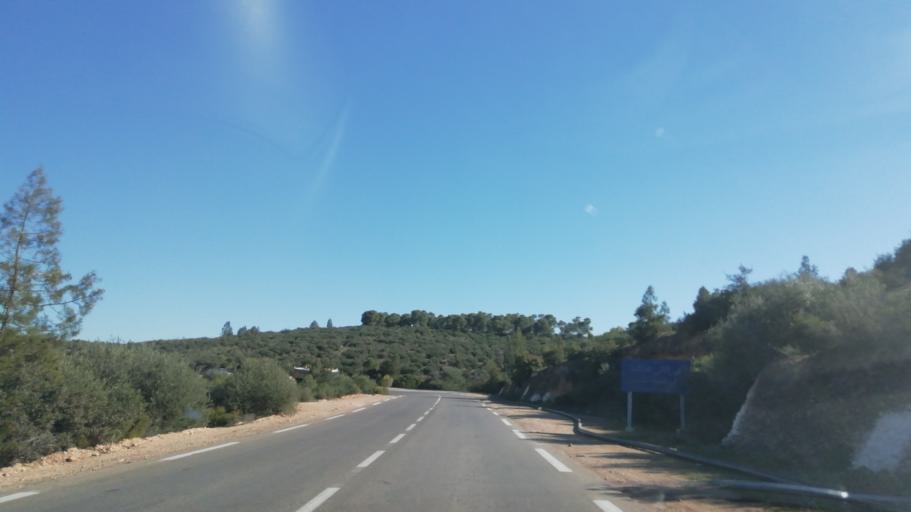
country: DZ
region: Tlemcen
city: Beni Mester
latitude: 34.8127
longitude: -1.6252
